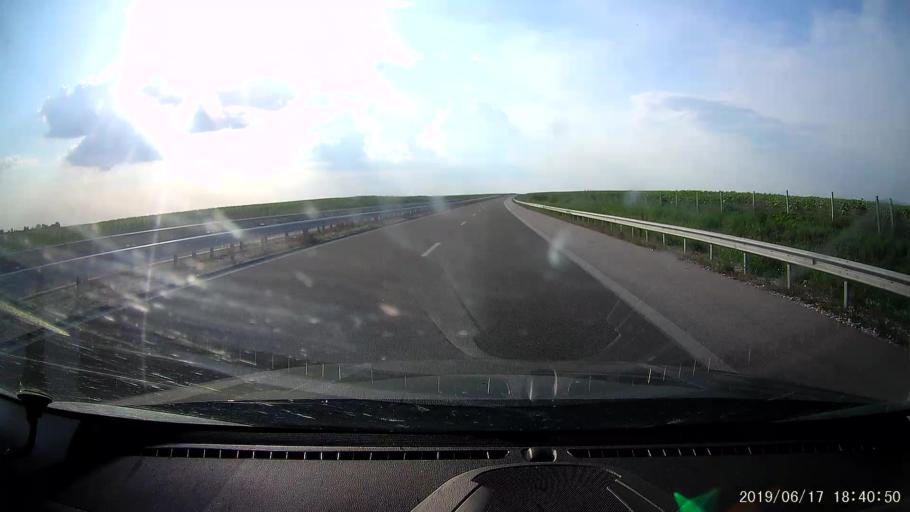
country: BG
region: Stara Zagora
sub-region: Obshtina Chirpan
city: Chirpan
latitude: 42.1614
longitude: 25.2679
